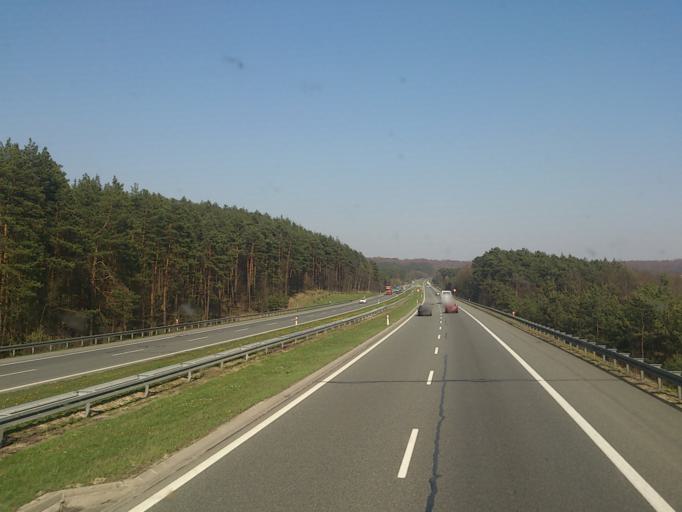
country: PL
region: Lesser Poland Voivodeship
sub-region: Powiat krakowski
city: Zalas
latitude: 50.0925
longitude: 19.6381
